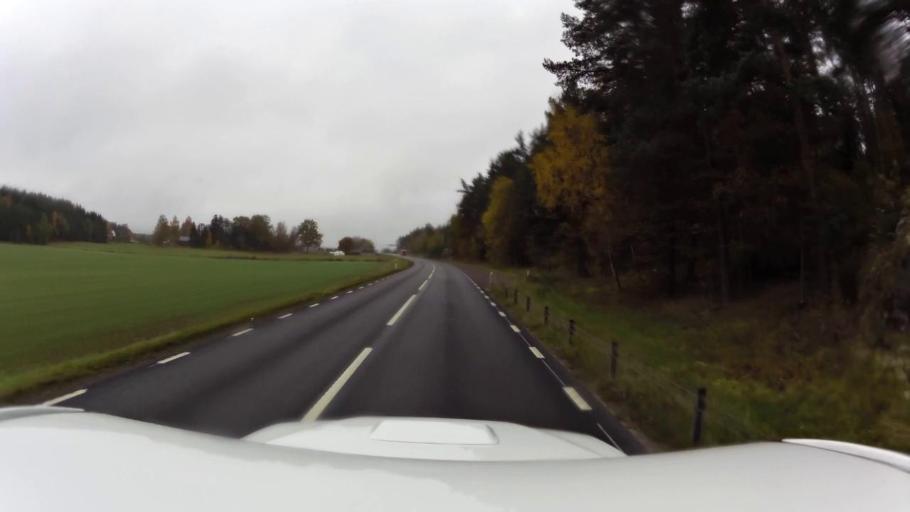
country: SE
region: OEstergoetland
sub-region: Linkopings Kommun
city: Linghem
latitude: 58.3593
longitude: 15.8285
